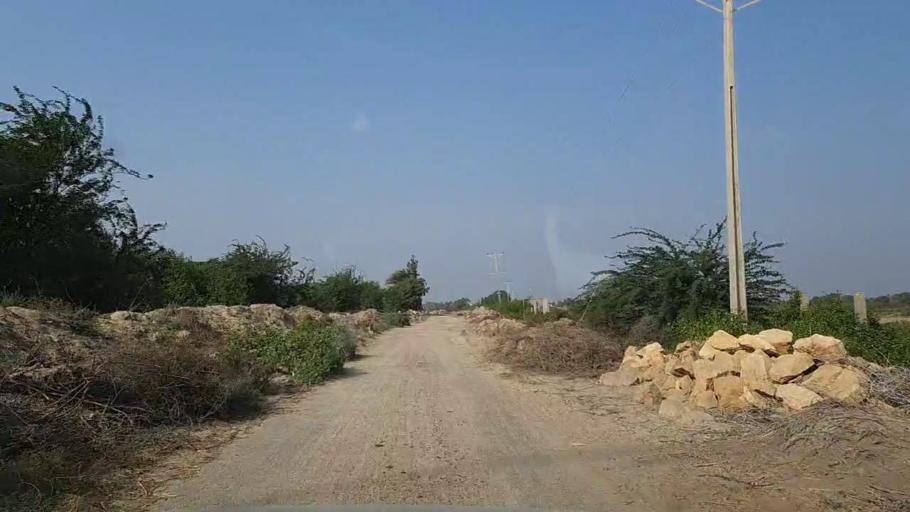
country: PK
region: Sindh
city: Mirpur Sakro
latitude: 24.5821
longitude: 67.5678
